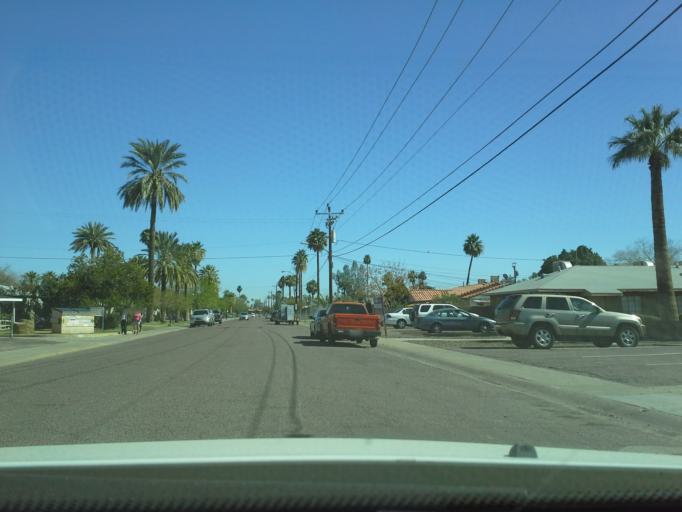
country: US
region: Arizona
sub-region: Maricopa County
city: Phoenix
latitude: 33.4999
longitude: -112.0644
